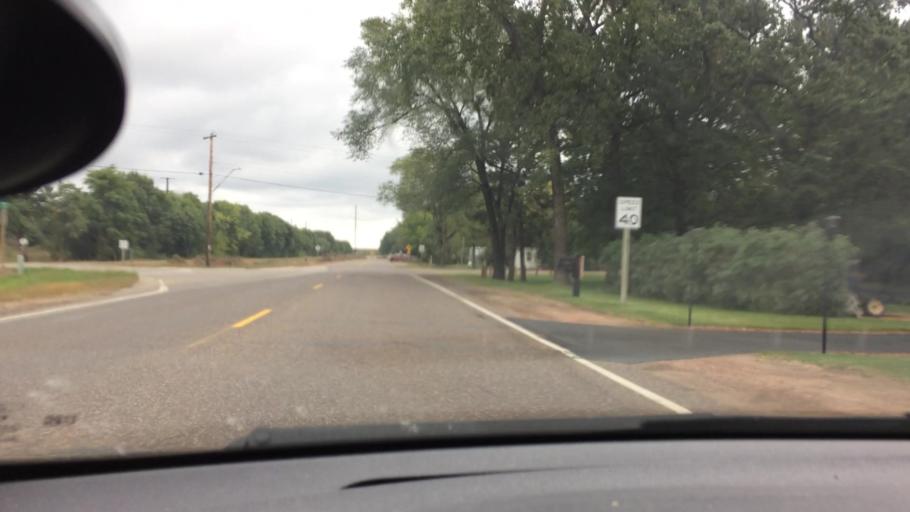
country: US
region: Wisconsin
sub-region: Chippewa County
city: Lake Hallie
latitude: 44.8858
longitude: -91.4294
